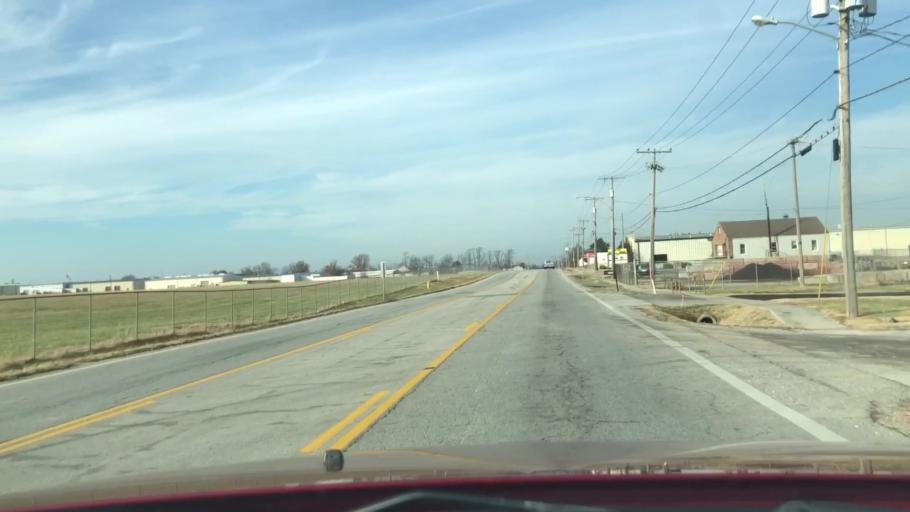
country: US
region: Missouri
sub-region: Greene County
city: Springfield
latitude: 37.2253
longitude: -93.2522
